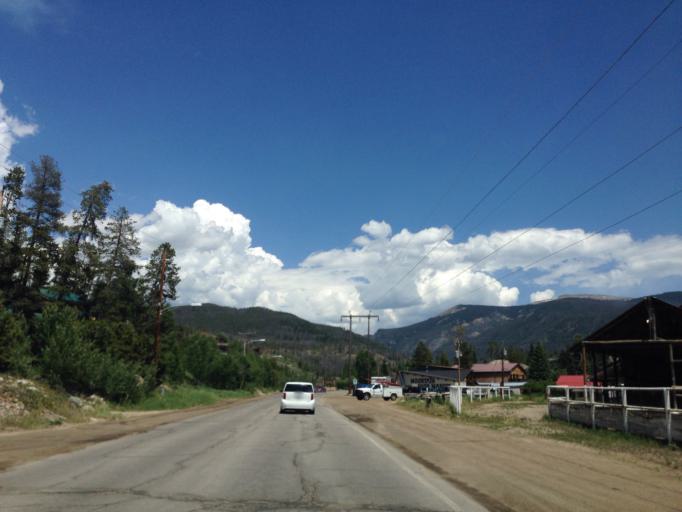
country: US
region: Colorado
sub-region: Grand County
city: Granby
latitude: 40.2527
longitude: -105.8309
